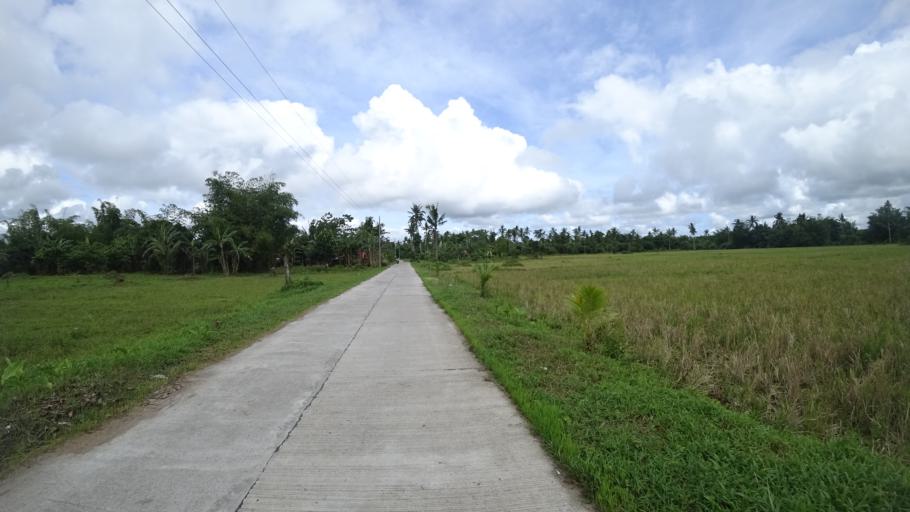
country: PH
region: Eastern Visayas
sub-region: Province of Leyte
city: Alangalang
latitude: 11.1728
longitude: 124.8602
